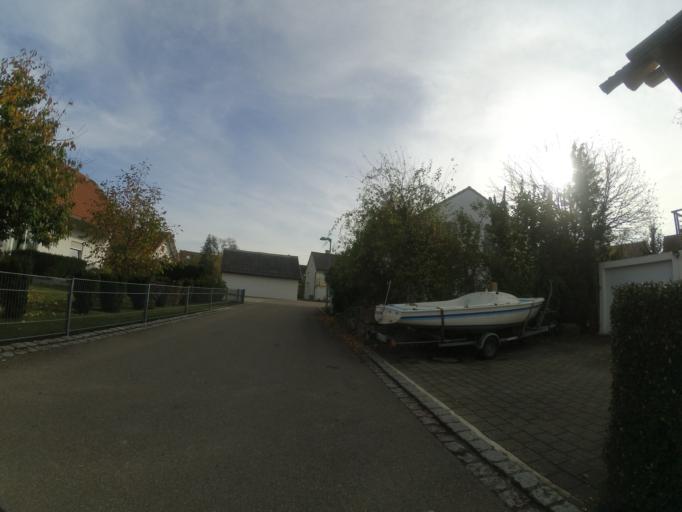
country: DE
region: Baden-Wuerttemberg
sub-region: Tuebingen Region
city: Blaubeuren
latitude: 48.4267
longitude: 9.8582
